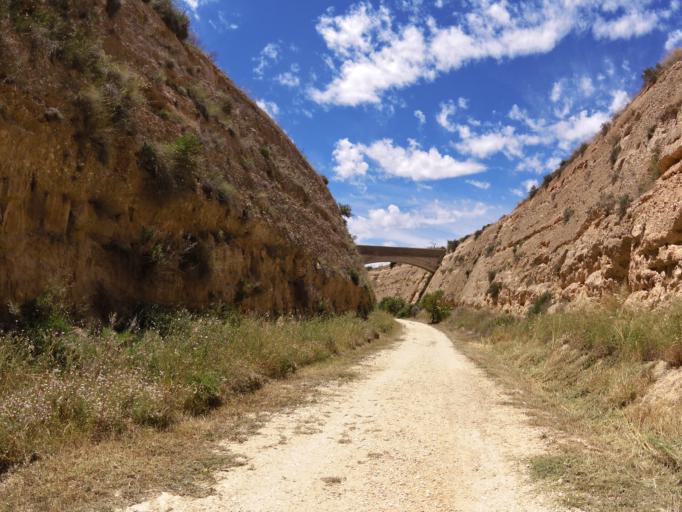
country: ES
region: Valencia
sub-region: Provincia de Alicante
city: Agost
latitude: 38.4517
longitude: -0.6710
